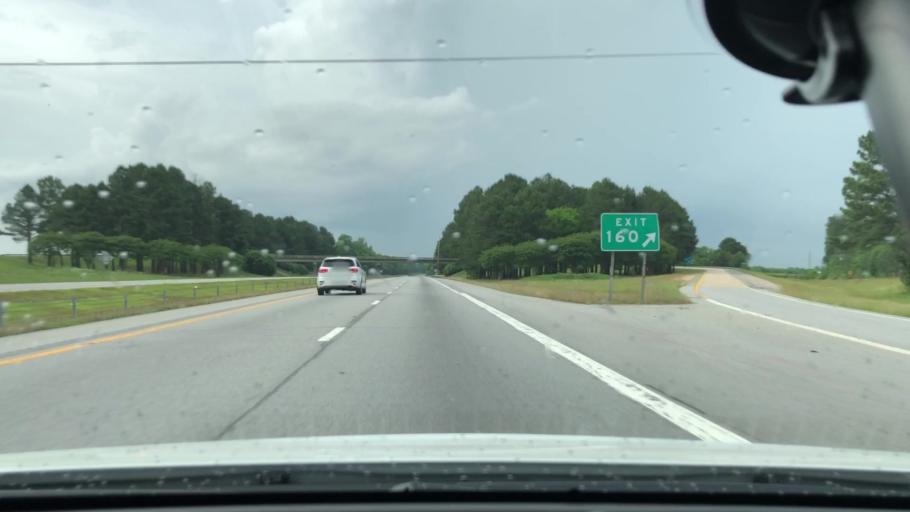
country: US
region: North Carolina
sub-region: Halifax County
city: Enfield
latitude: 36.2664
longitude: -77.7230
